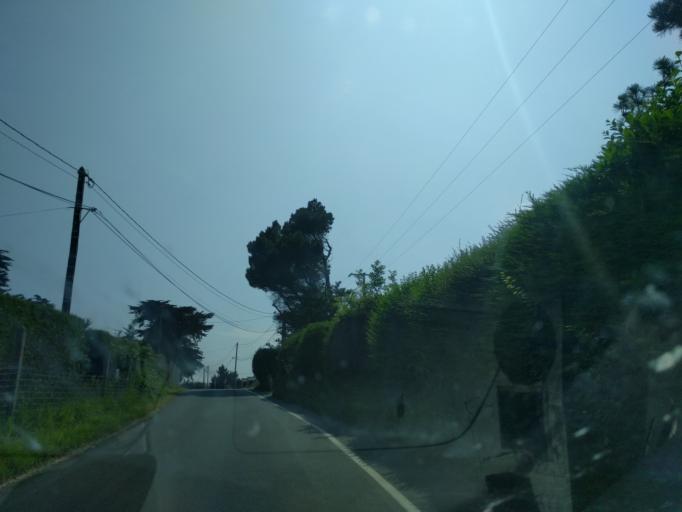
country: FR
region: Brittany
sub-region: Departement des Cotes-d'Armor
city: Plurien
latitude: 48.6433
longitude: -2.4231
